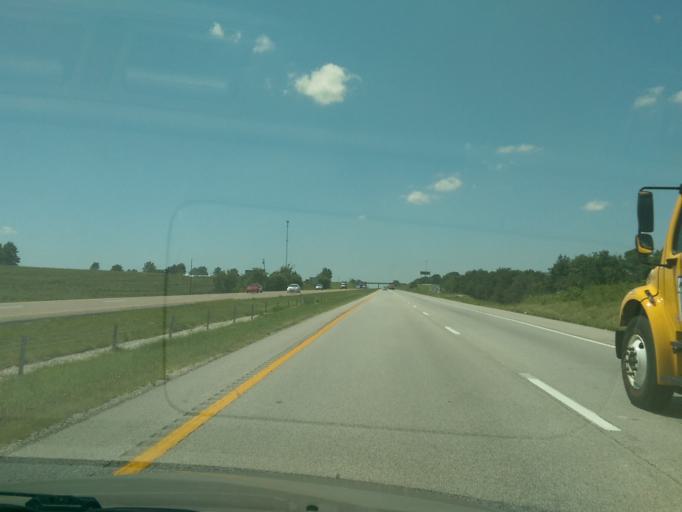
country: US
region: Missouri
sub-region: Cooper County
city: Boonville
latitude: 38.9353
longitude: -92.8054
